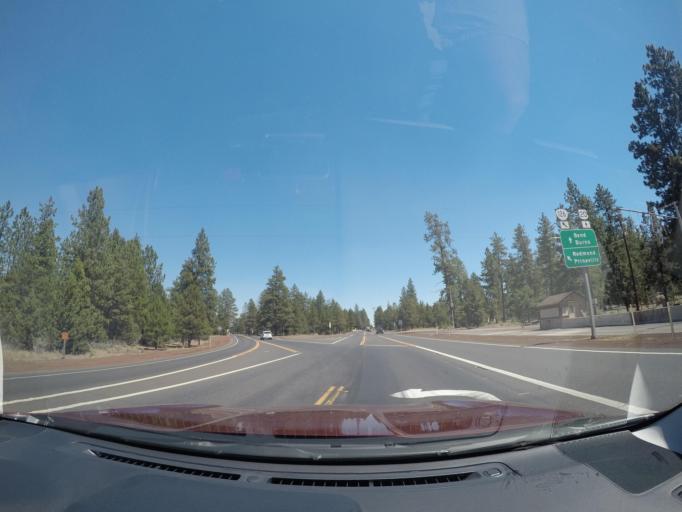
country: US
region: Oregon
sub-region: Deschutes County
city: Sisters
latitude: 44.2879
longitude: -121.5404
